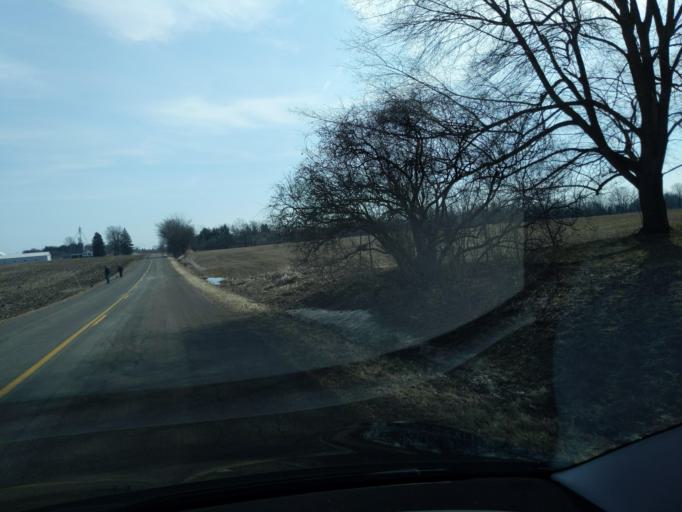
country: US
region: Michigan
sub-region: Ingham County
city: Williamston
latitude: 42.6588
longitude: -84.2708
